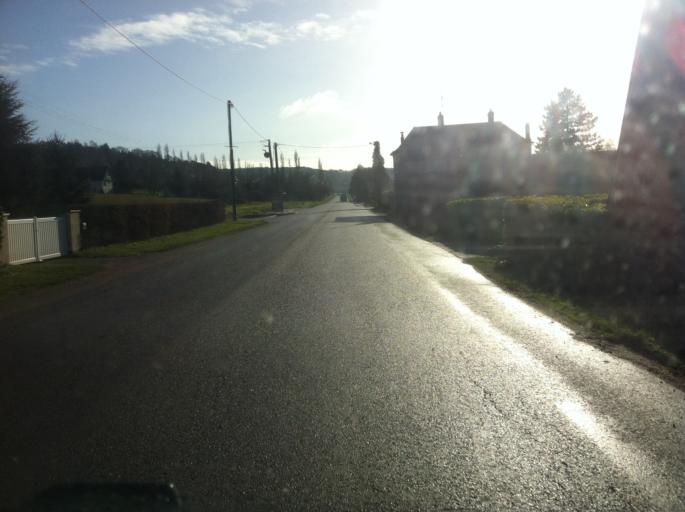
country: FR
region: Haute-Normandie
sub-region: Departement de la Seine-Maritime
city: Saint-Martin-de-Boscherville
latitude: 49.4581
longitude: 0.9587
